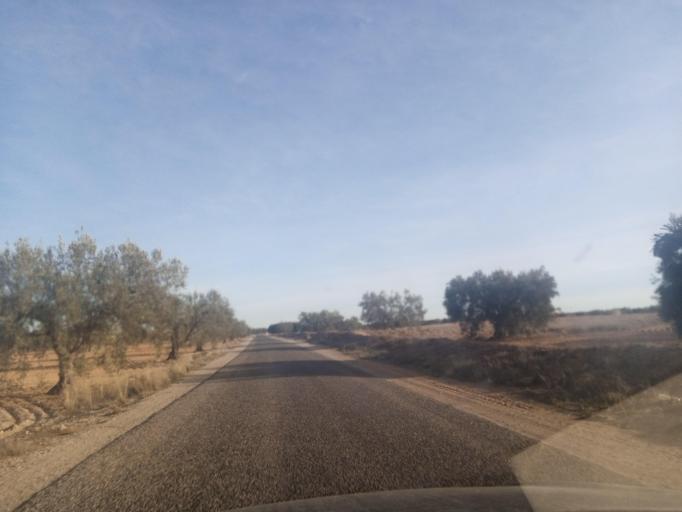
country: TN
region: Safaqis
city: Bi'r `Ali Bin Khalifah
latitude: 34.8896
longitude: 10.1786
